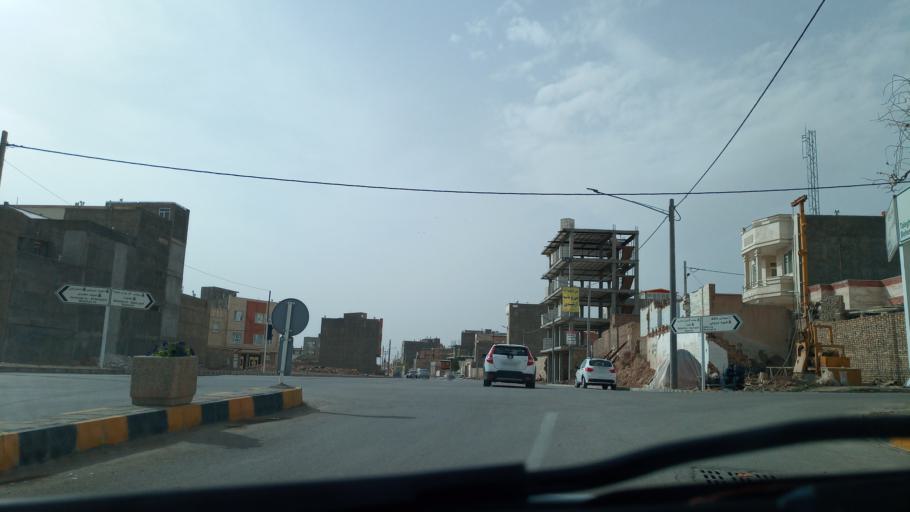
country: IR
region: Khorasan-e Shomali
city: Esfarayen
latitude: 37.0822
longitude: 57.5097
